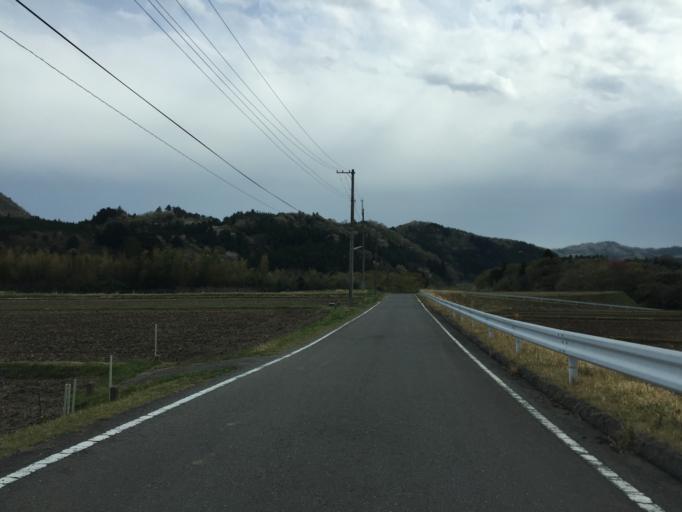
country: JP
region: Fukushima
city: Iwaki
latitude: 37.1383
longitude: 140.9052
